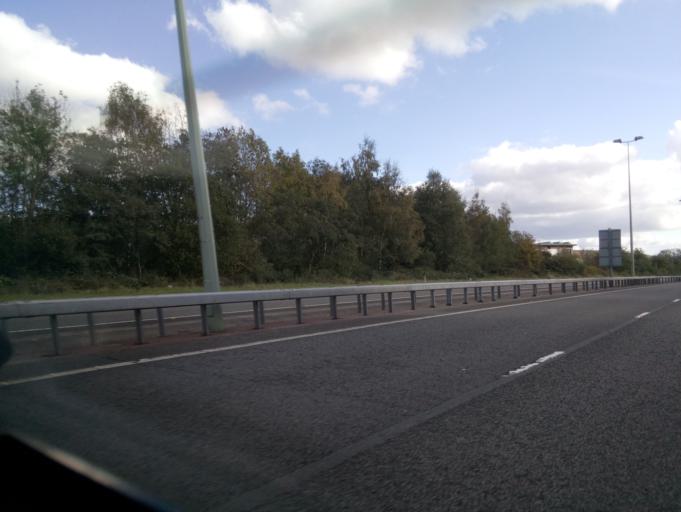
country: GB
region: Wales
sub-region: Merthyr Tydfil County Borough
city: Merthyr Tydfil
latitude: 51.7469
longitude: -3.3923
